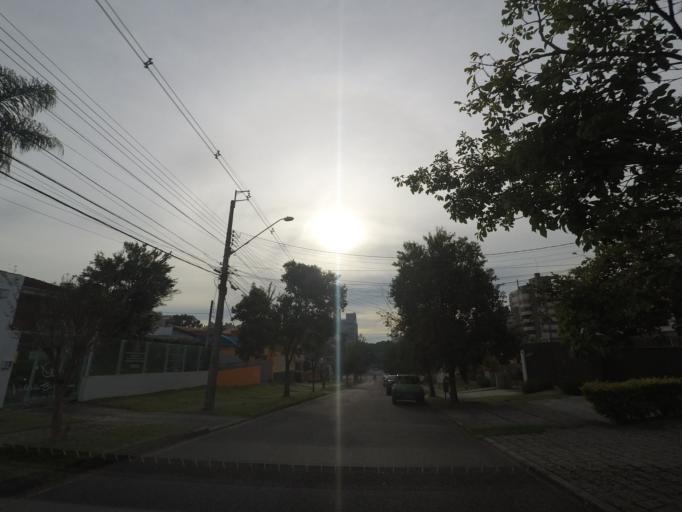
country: BR
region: Parana
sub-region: Curitiba
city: Curitiba
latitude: -25.4357
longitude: -49.2944
